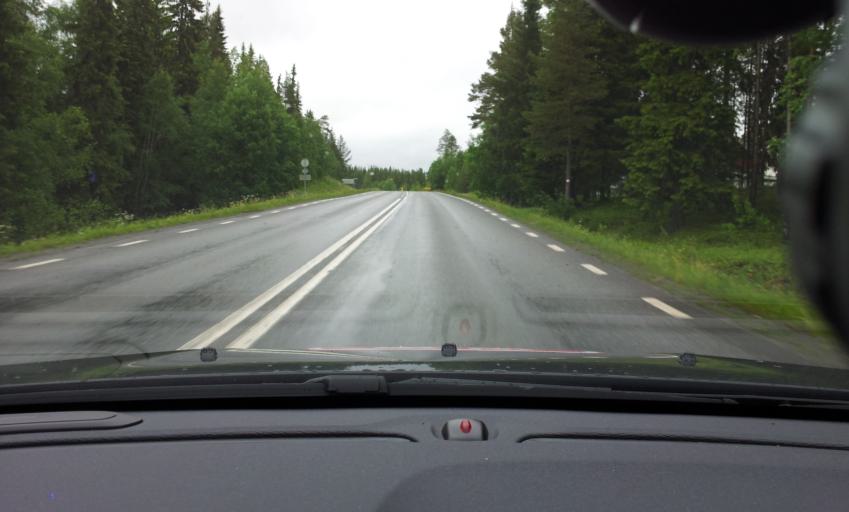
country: SE
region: Jaemtland
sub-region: Krokoms Kommun
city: Krokom
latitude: 63.3393
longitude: 14.4638
